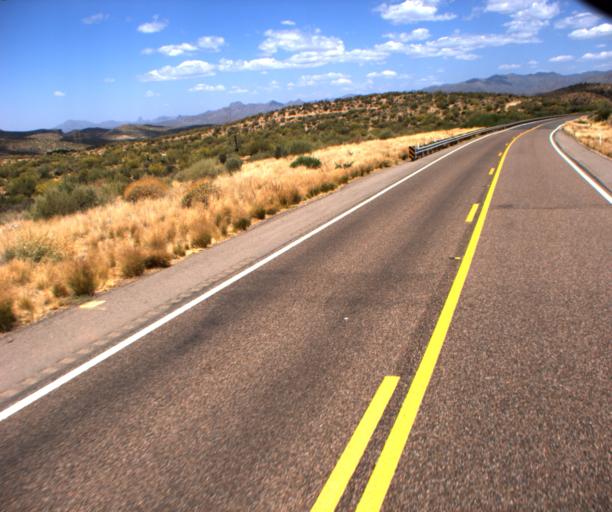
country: US
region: Arizona
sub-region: Pinal County
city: Superior
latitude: 33.2409
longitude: -111.0956
